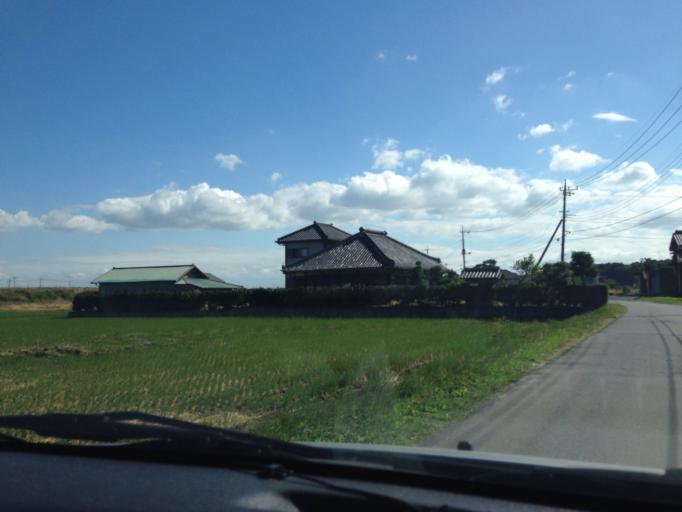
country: JP
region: Ibaraki
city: Inashiki
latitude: 36.0245
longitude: 140.2964
